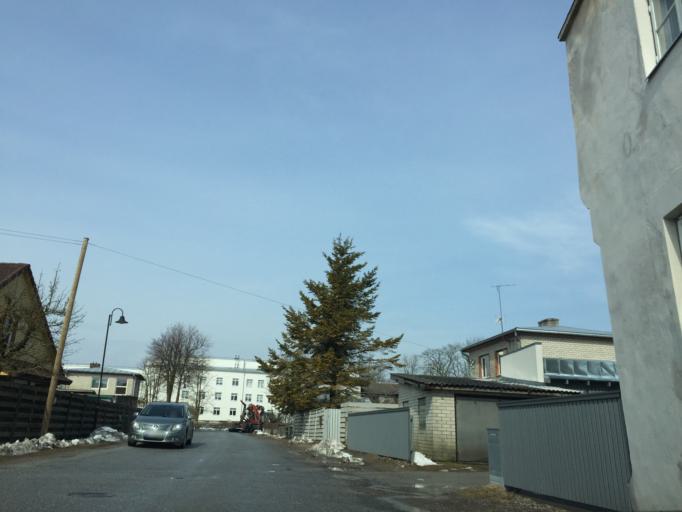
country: EE
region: Saare
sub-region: Kuressaare linn
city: Kuressaare
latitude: 58.2507
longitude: 22.4751
